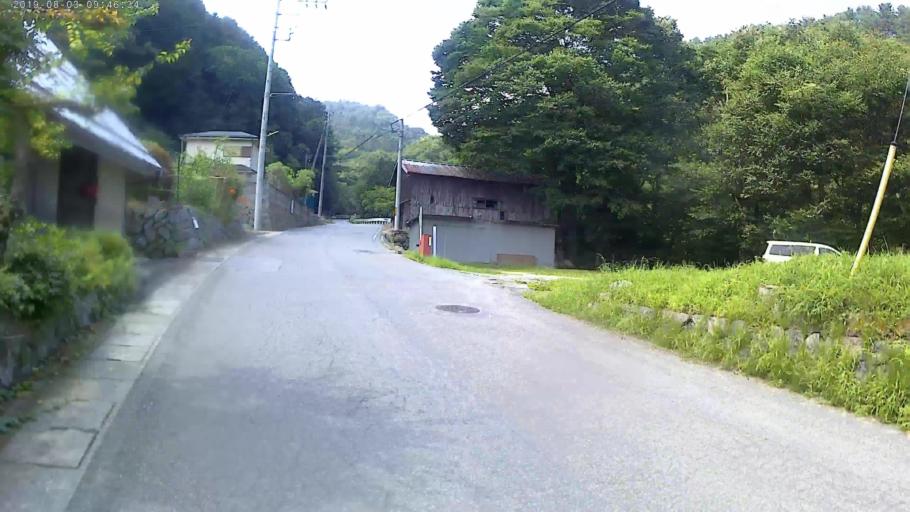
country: JP
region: Yamanashi
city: Enzan
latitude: 35.6356
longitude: 138.7694
